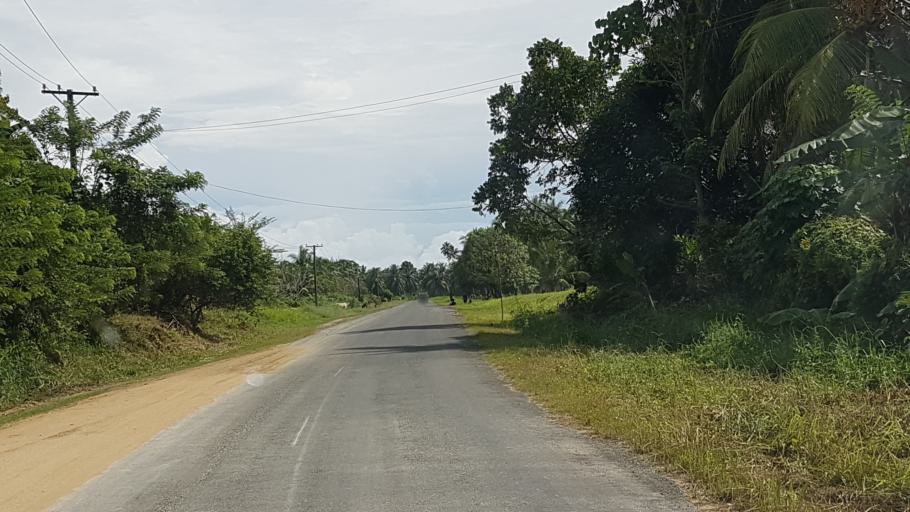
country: PG
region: Madang
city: Madang
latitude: -4.9764
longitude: 145.7764
